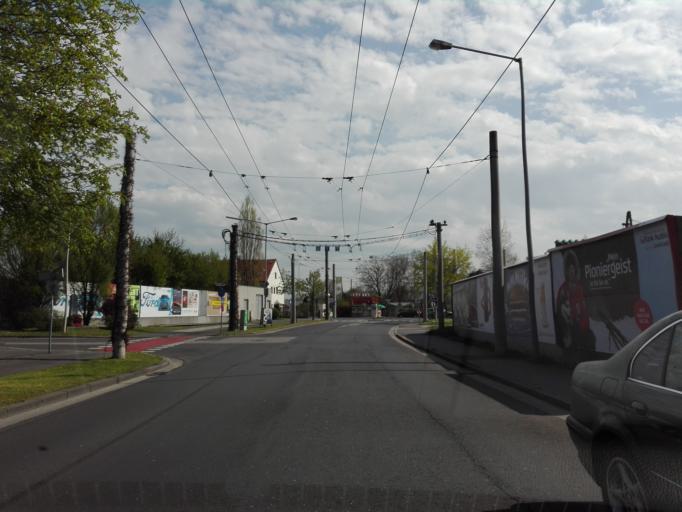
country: AT
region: Upper Austria
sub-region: Politischer Bezirk Linz-Land
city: Ansfelden
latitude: 48.2470
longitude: 14.2862
